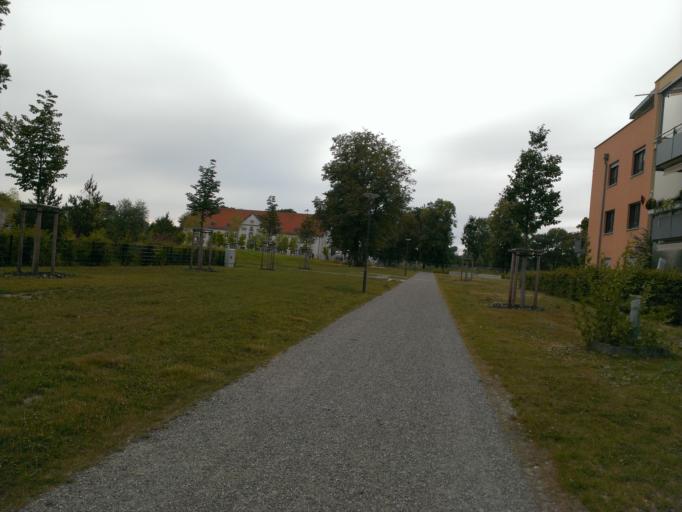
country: DE
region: Bavaria
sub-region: Swabia
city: Stadtbergen
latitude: 48.3626
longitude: 10.8606
